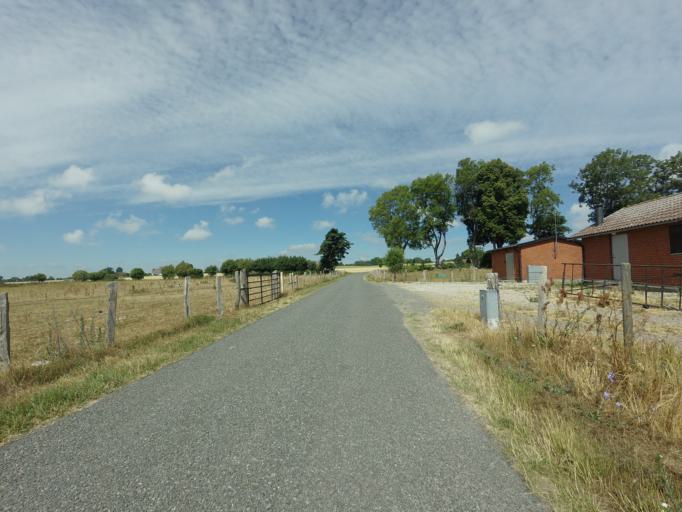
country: SE
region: Skane
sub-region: Simrishamns Kommun
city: Simrishamn
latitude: 55.4883
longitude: 14.3122
